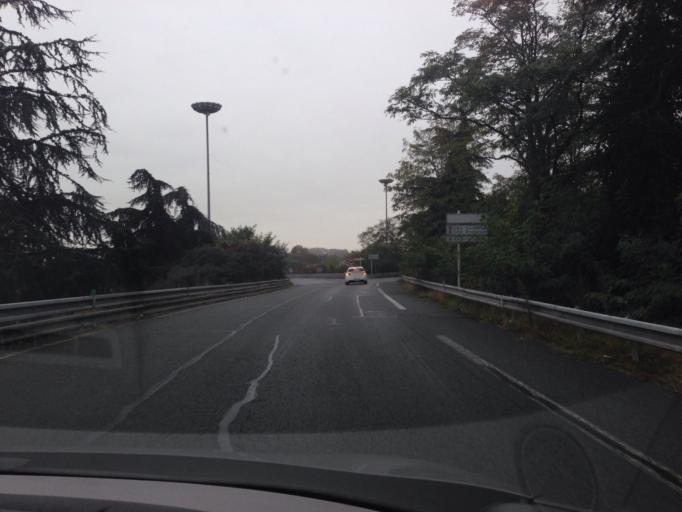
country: FR
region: Centre
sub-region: Departement d'Indre-et-Loire
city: Tours
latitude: 47.3962
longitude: 0.7069
